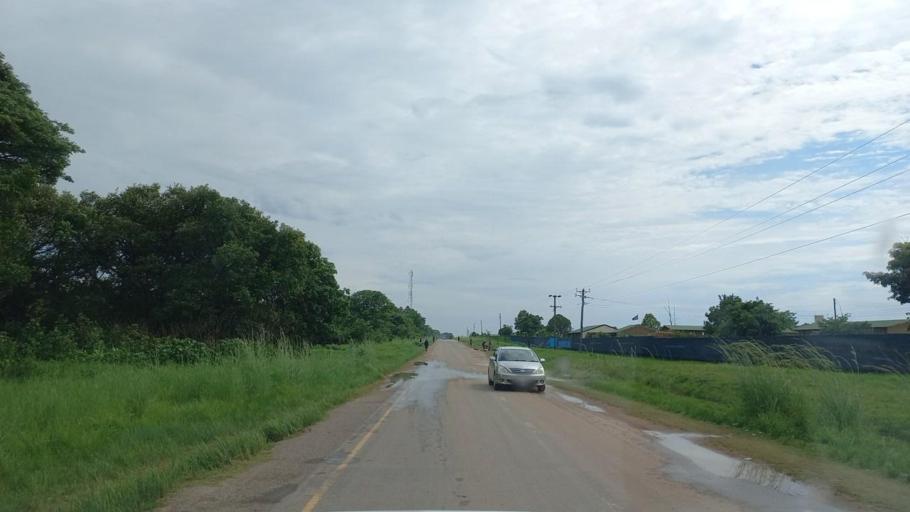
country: ZM
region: Copperbelt
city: Kitwe
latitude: -12.8768
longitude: 28.3273
